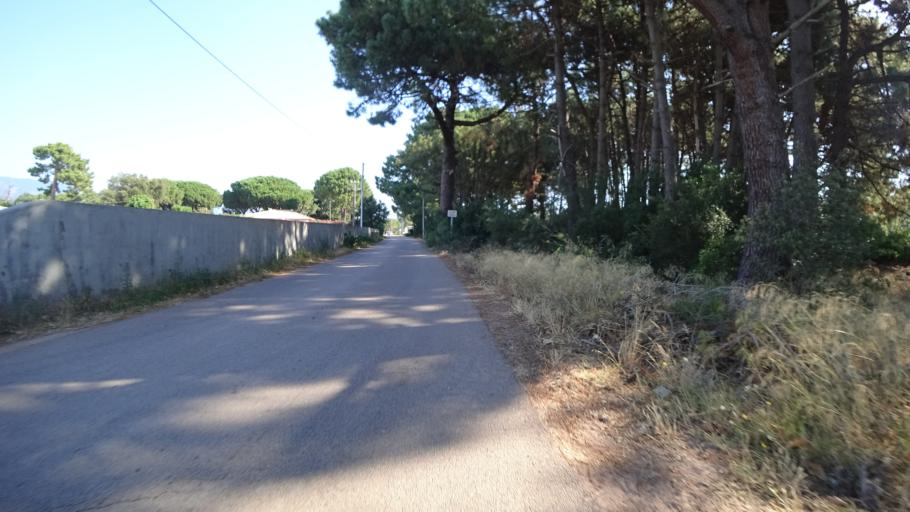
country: FR
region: Corsica
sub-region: Departement de la Corse-du-Sud
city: Porto-Vecchio
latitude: 41.6310
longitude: 9.3309
